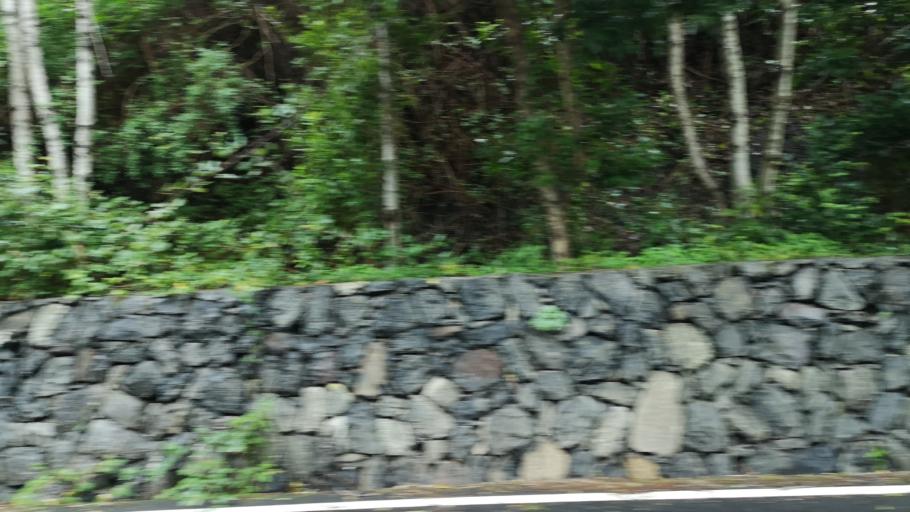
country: ES
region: Canary Islands
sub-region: Provincia de Santa Cruz de Tenerife
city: Hermigua
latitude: 28.1281
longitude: -17.2112
